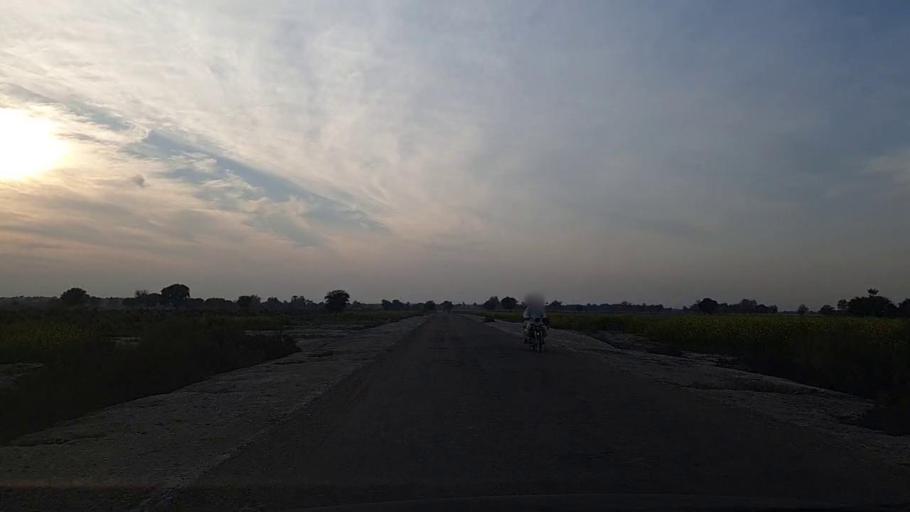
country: PK
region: Sindh
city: Jam Sahib
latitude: 26.4029
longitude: 68.4923
